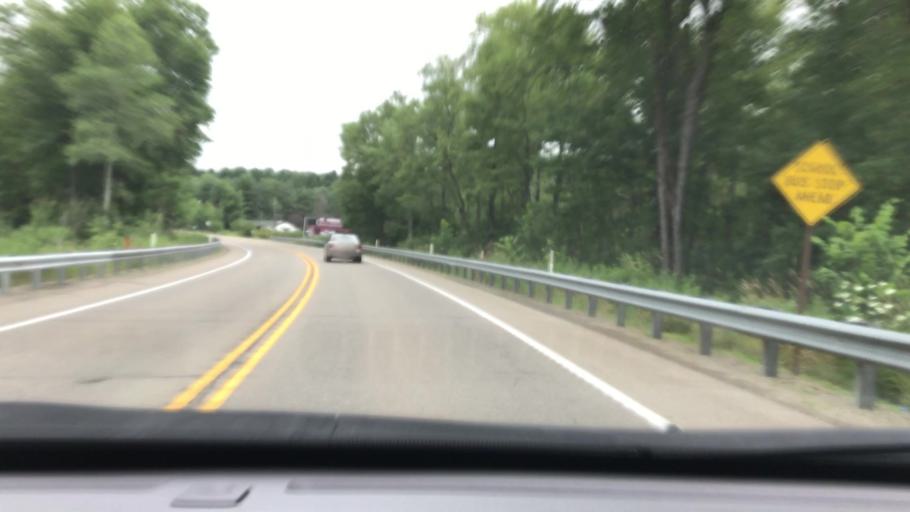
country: US
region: Pennsylvania
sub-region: Elk County
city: Johnsonburg
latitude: 41.5249
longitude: -78.6753
